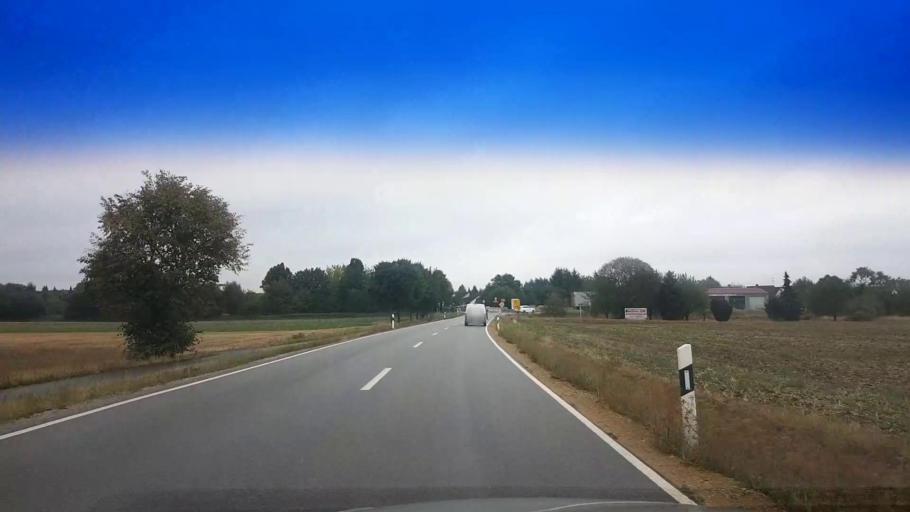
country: DE
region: Bavaria
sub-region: Upper Franconia
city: Eggolsheim
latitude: 49.7767
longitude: 11.0509
